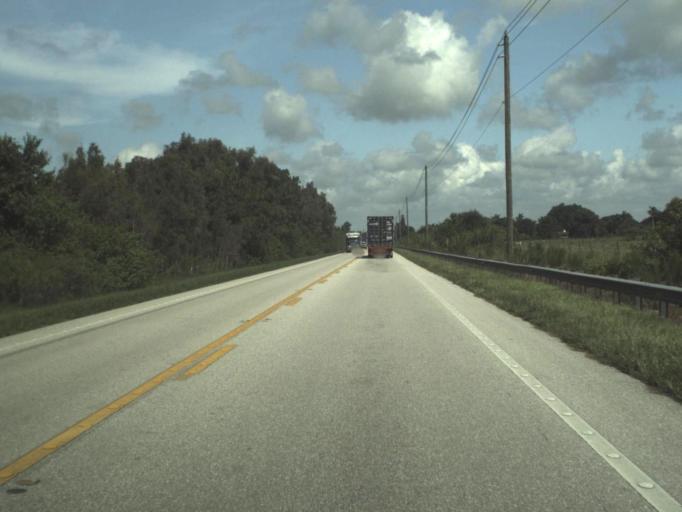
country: US
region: Florida
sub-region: Martin County
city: Indiantown
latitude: 27.0810
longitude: -80.5595
